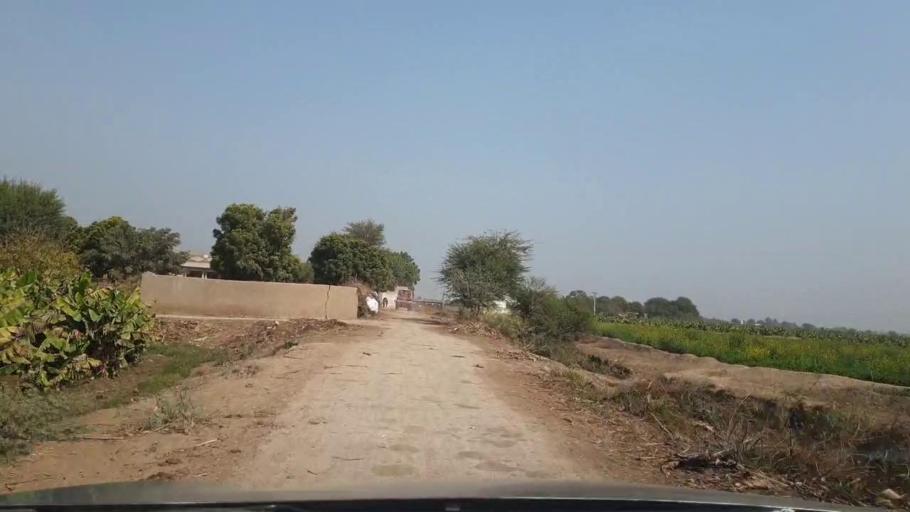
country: PK
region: Sindh
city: Tando Allahyar
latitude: 25.5390
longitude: 68.7858
